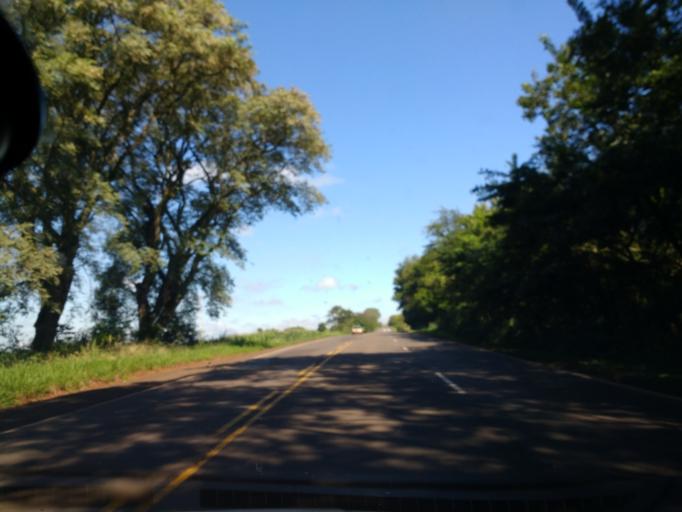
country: BR
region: Parana
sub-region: Terra Boa
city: Terra Boa
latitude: -23.6194
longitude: -52.4372
